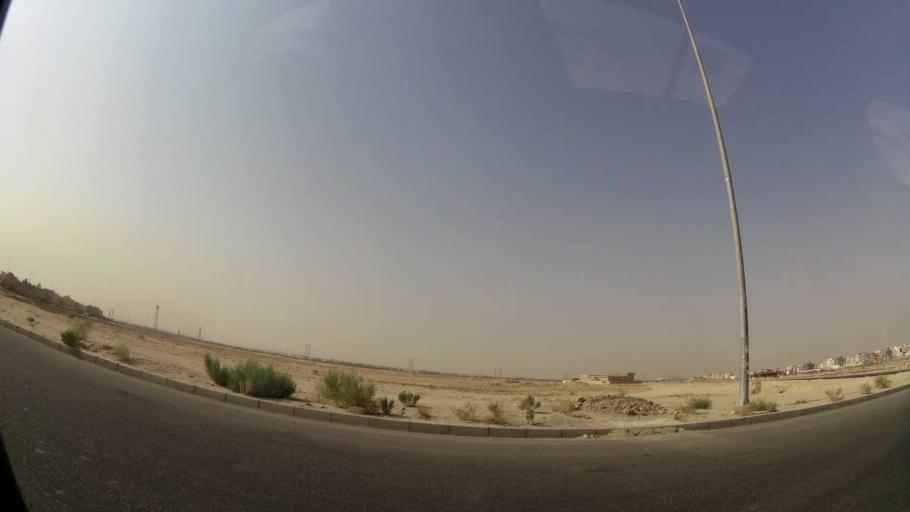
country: KW
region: Muhafazat al Jahra'
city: Al Jahra'
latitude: 29.3416
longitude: 47.7607
